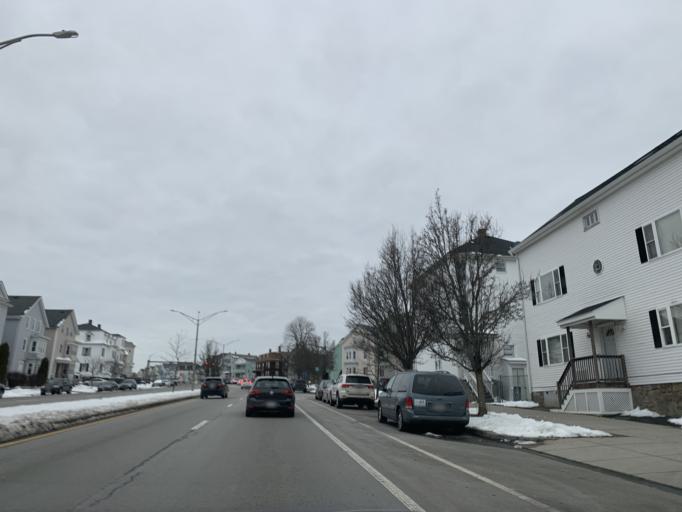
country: US
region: Massachusetts
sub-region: Bristol County
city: Fall River
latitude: 41.6936
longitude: -71.1557
